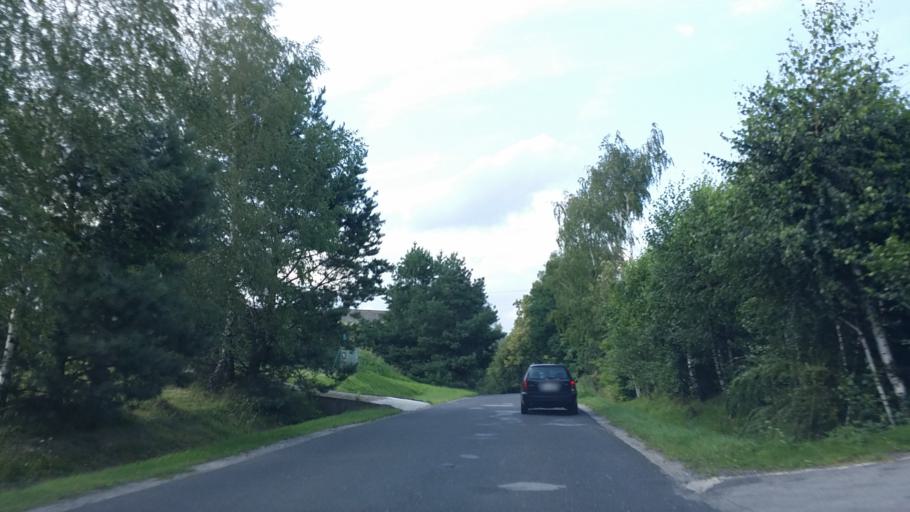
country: PL
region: Lesser Poland Voivodeship
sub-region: Powiat myslenicki
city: Brzaczowice
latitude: 49.9061
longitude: 20.0350
